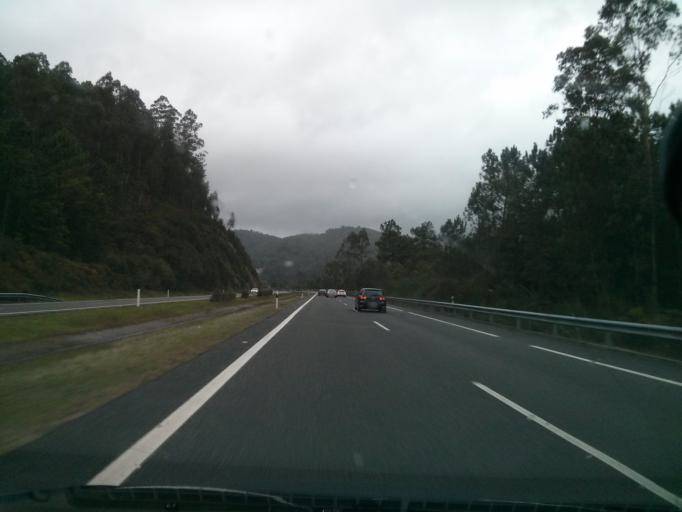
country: ES
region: Galicia
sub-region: Provincia de Pontevedra
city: Ponteareas
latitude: 42.1736
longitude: -8.5556
